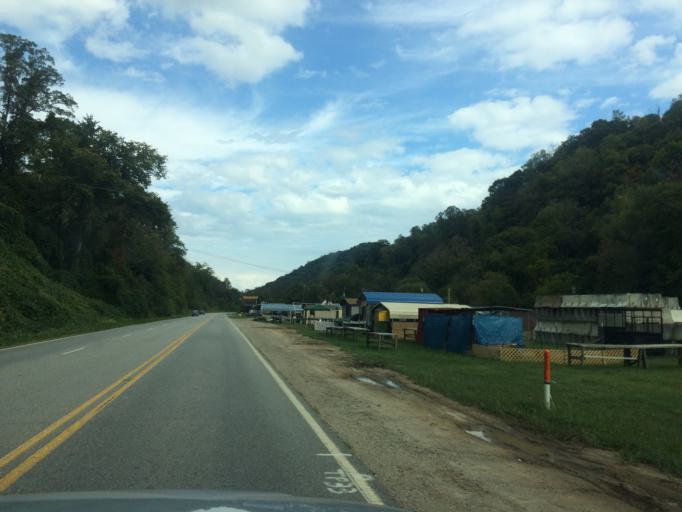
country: US
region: North Carolina
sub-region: Haywood County
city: Canton
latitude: 35.5363
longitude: -82.8031
